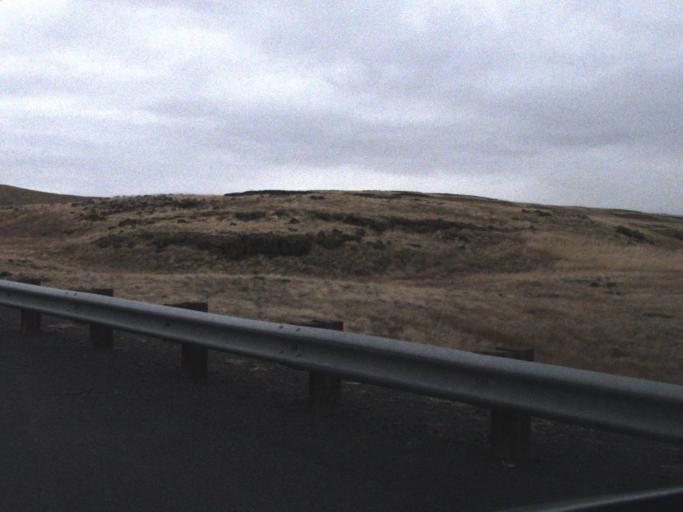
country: US
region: Washington
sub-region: Adams County
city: Ritzville
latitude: 46.7698
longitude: -118.1501
